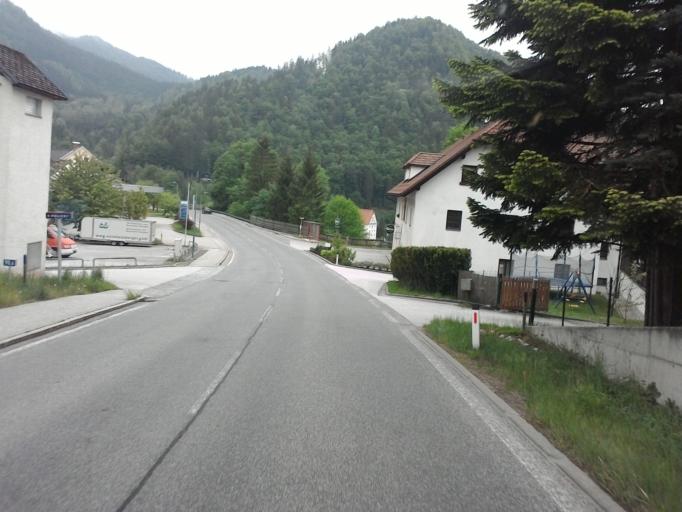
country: AT
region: Styria
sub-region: Politischer Bezirk Liezen
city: Landl
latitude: 47.6659
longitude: 14.7172
